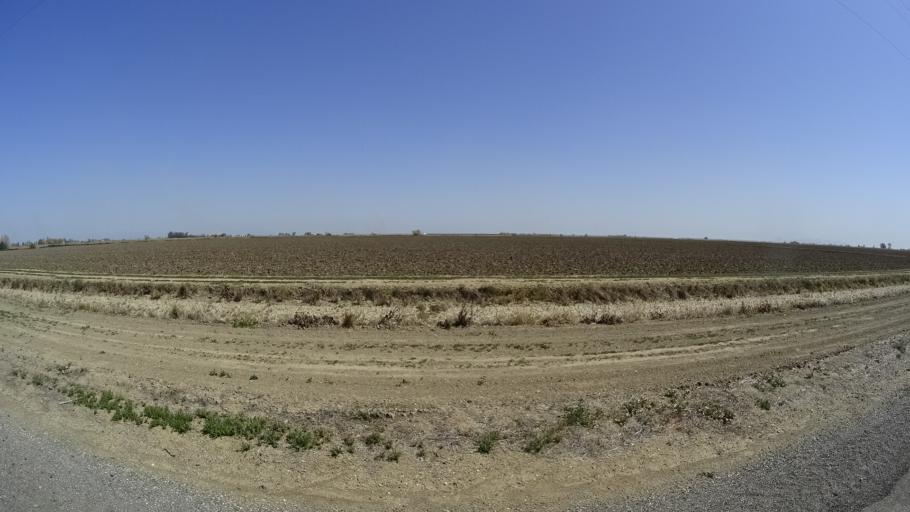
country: US
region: California
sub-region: Glenn County
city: Willows
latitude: 39.5135
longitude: -122.1368
